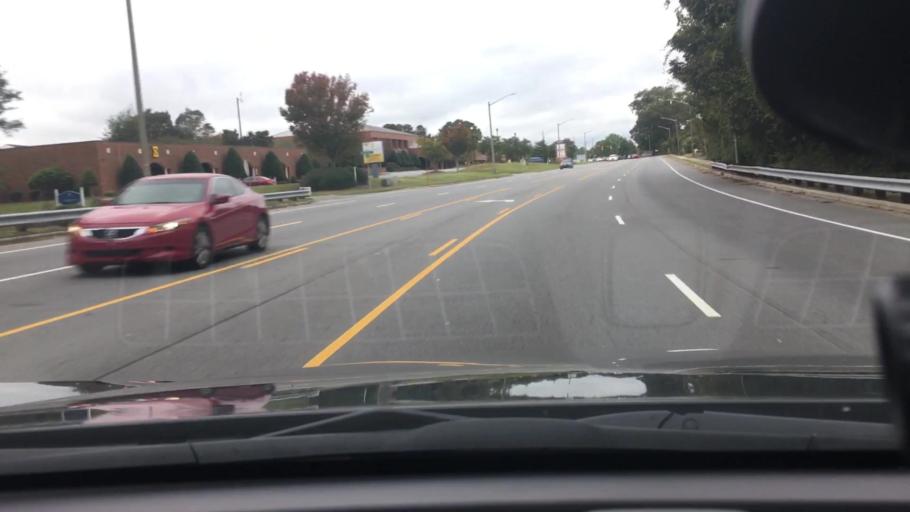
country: US
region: North Carolina
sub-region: Pitt County
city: Summerfield
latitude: 35.5925
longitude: -77.3992
